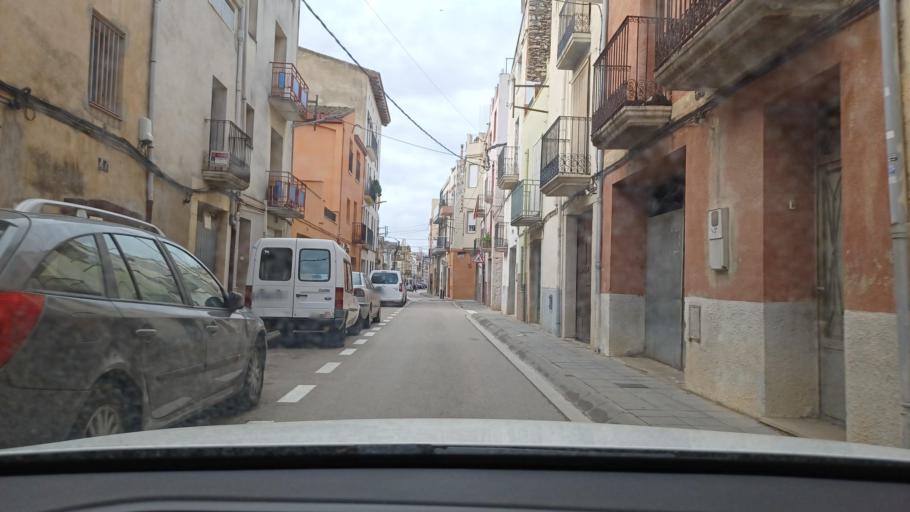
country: ES
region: Catalonia
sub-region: Provincia de Tarragona
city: Ulldecona
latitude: 40.5981
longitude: 0.4460
